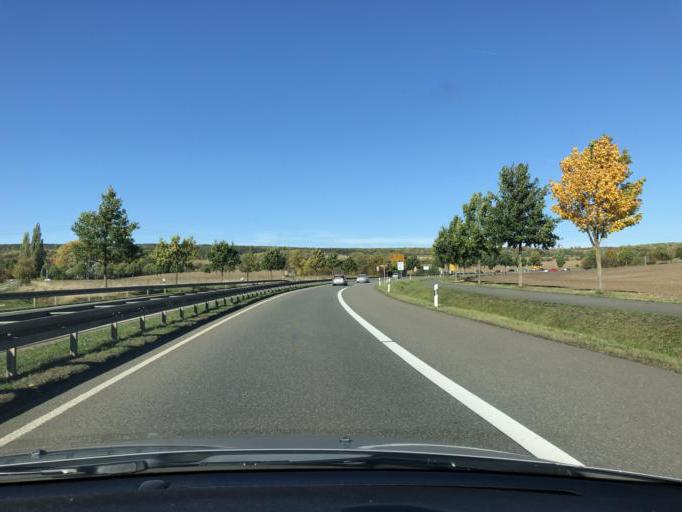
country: DE
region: Thuringia
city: Hopfgarten
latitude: 50.9910
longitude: 11.2885
